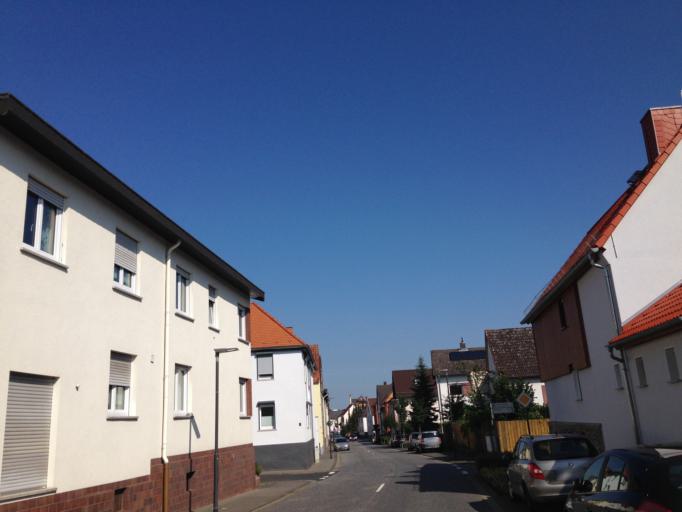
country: DE
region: Hesse
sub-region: Regierungsbezirk Giessen
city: Langgons
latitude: 50.5252
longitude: 8.6748
